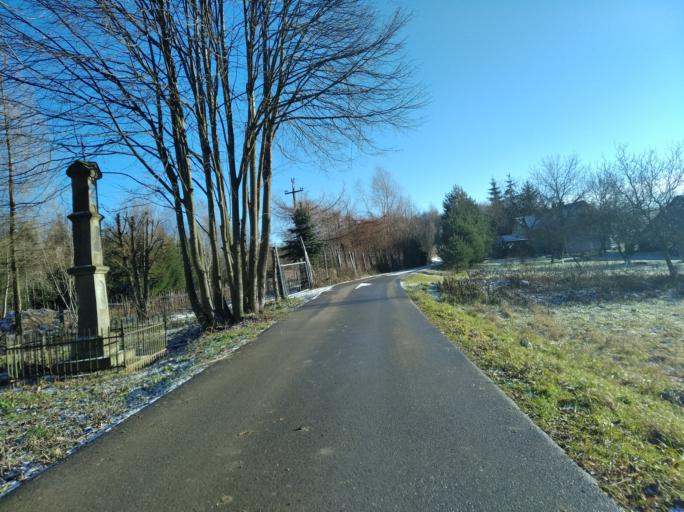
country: PL
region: Subcarpathian Voivodeship
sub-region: Powiat ropczycko-sedziszowski
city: Iwierzyce
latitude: 49.9565
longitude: 21.7565
